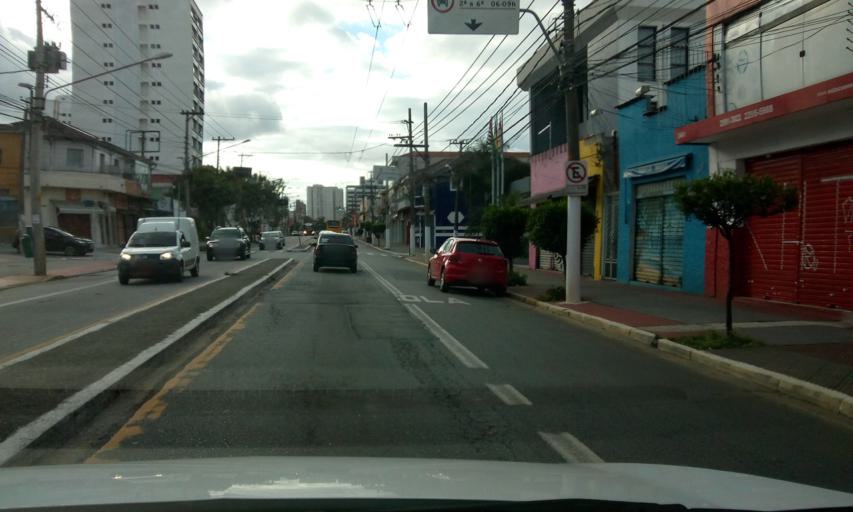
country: BR
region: Sao Paulo
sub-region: Sao Caetano Do Sul
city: Sao Caetano do Sul
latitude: -23.5484
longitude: -46.5377
